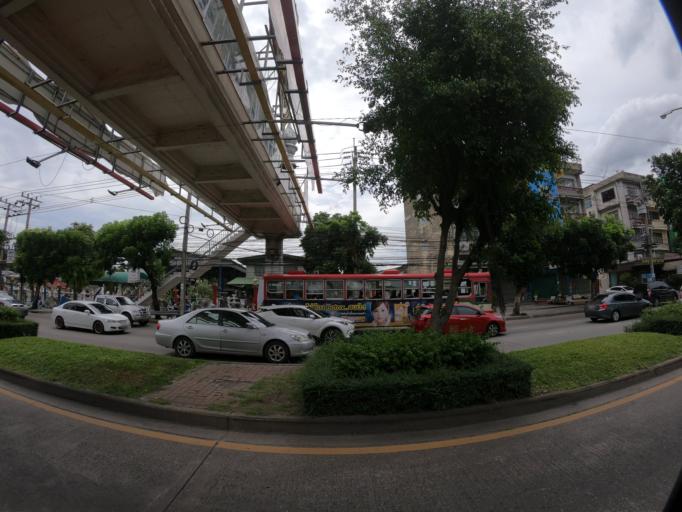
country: TH
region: Bangkok
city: Khan Na Yao
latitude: 13.8141
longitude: 100.6519
